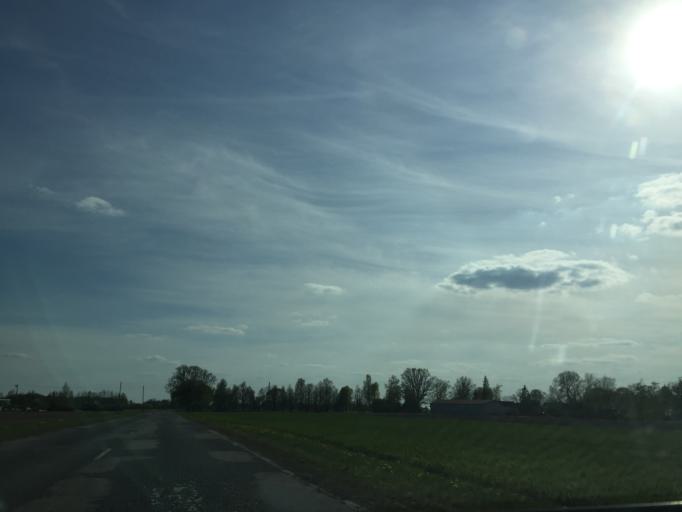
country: LV
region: Bauskas Rajons
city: Bauska
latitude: 56.4292
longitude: 24.2315
